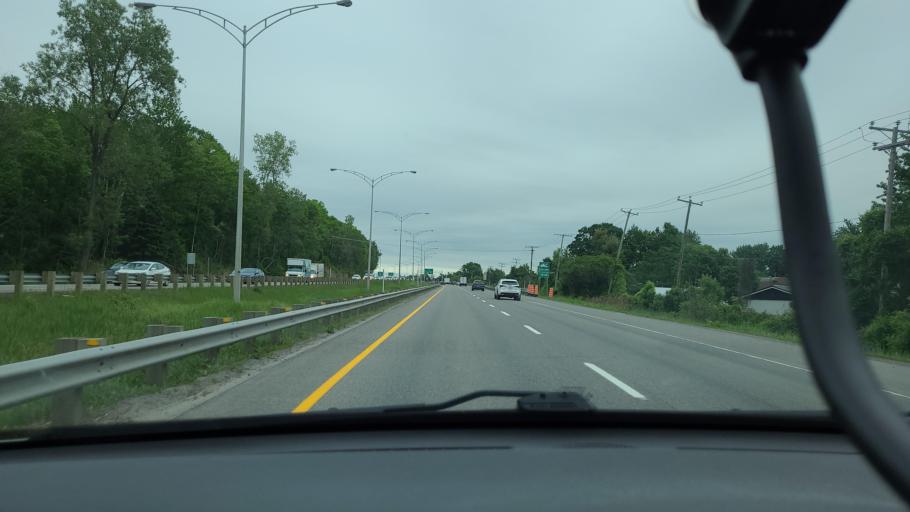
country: CA
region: Quebec
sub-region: Lanaudiere
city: Terrebonne
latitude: 45.7093
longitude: -73.6406
